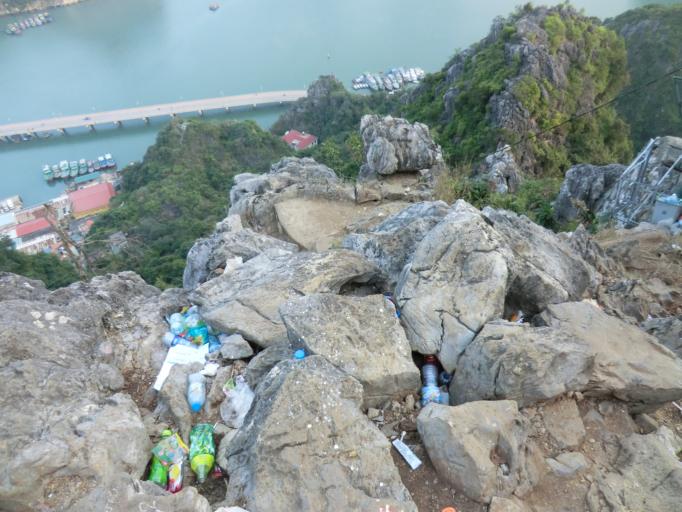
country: VN
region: Quang Ninh
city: Thanh Pho Ha Long
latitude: 20.9482
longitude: 107.0785
